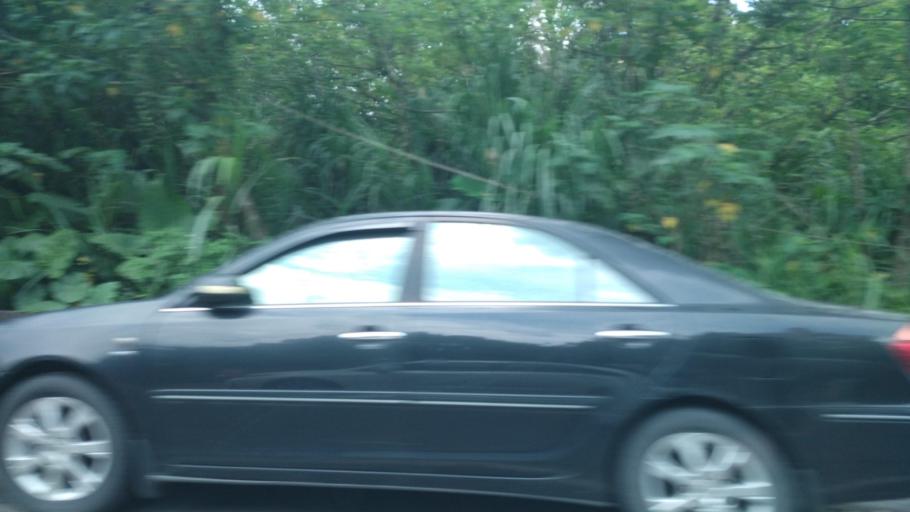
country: TW
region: Taipei
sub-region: Taipei
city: Banqiao
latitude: 24.9438
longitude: 121.4756
